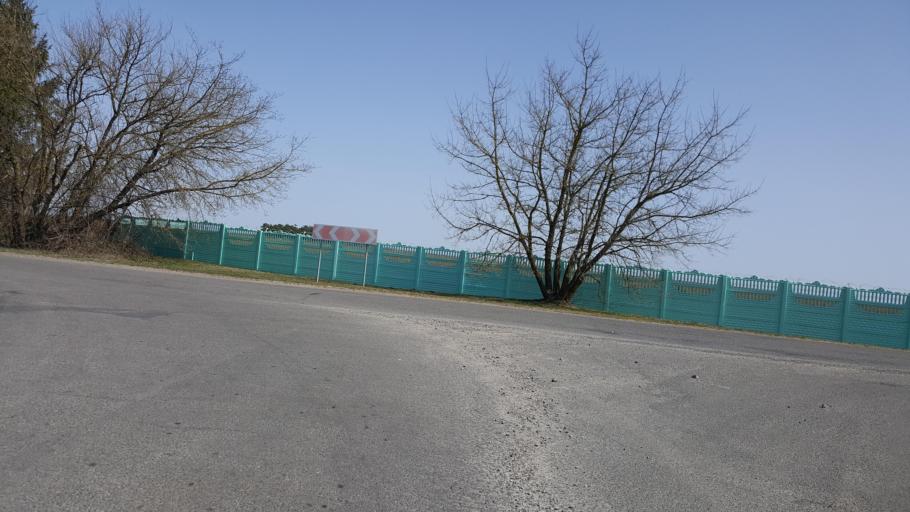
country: BY
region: Brest
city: Kamyanyets
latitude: 52.4118
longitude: 23.7892
